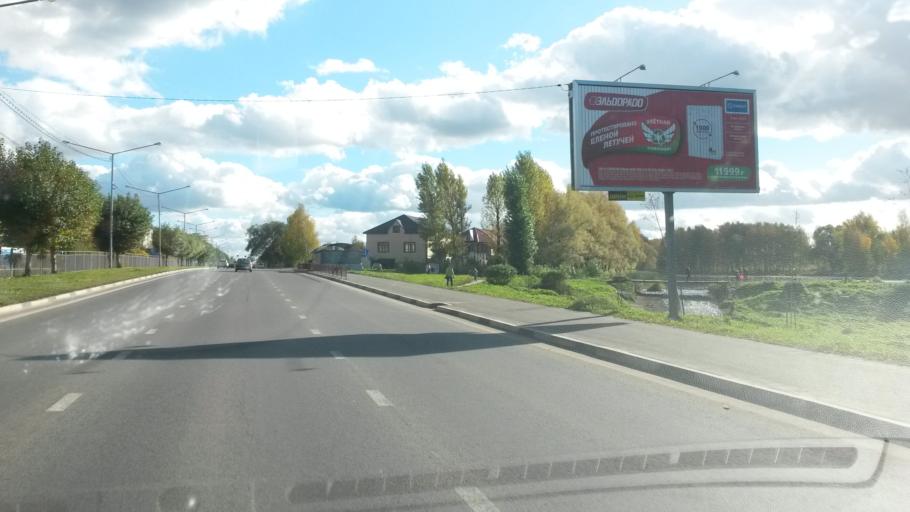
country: RU
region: Jaroslavl
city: Yaroslavl
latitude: 57.5741
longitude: 39.9195
